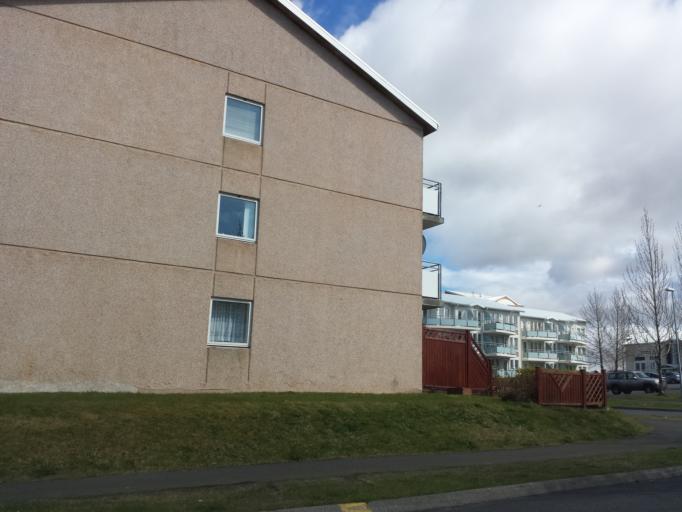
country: IS
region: Capital Region
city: Kopavogur
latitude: 64.1039
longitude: -21.8868
